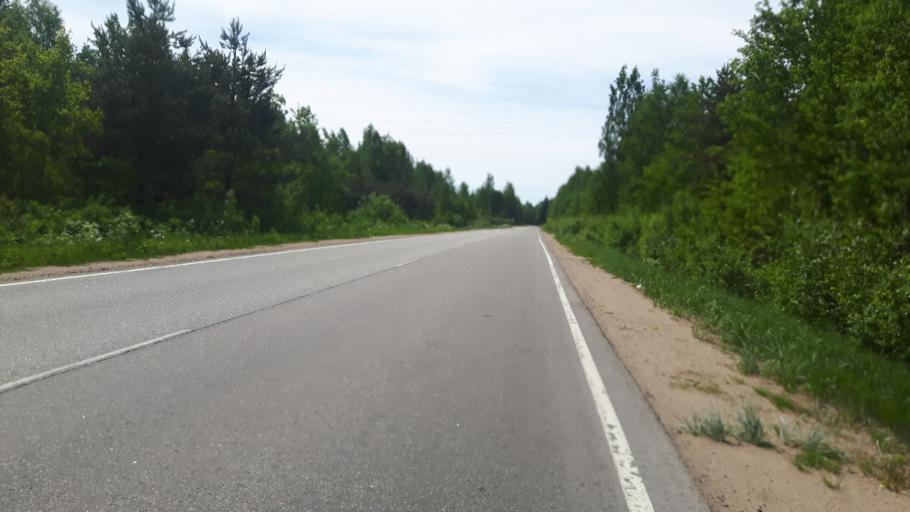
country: RU
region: Leningrad
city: Ust'-Luga
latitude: 59.6546
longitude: 28.2435
